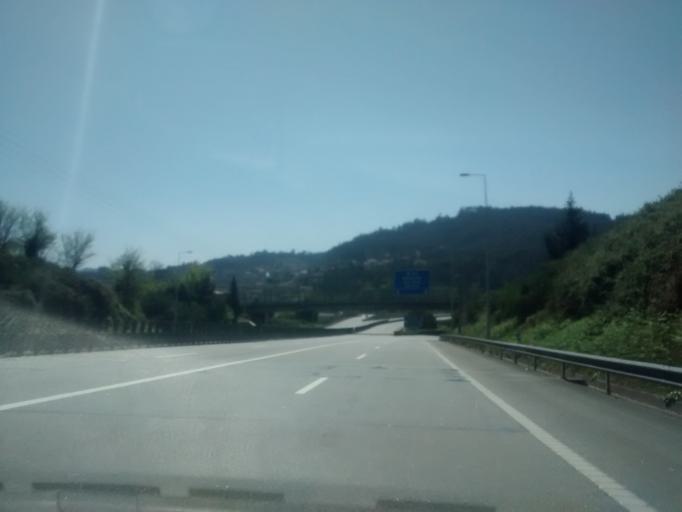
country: PT
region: Braga
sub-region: Braga
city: Oliveira
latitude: 41.5107
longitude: -8.4448
